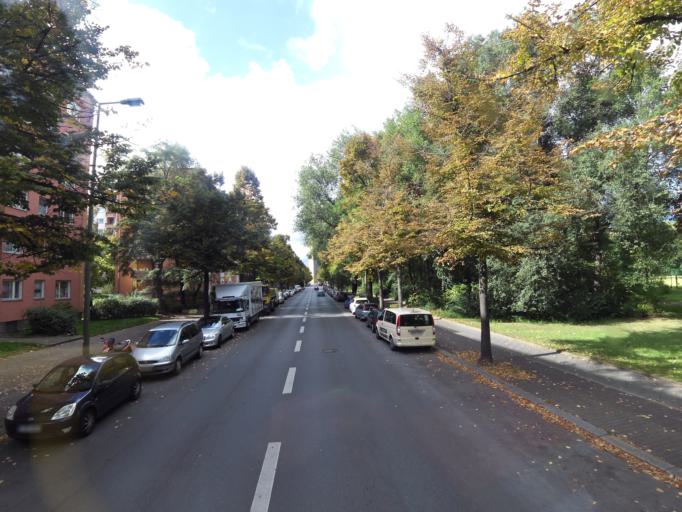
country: DE
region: Berlin
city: Bezirk Kreuzberg
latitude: 52.5054
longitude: 13.4045
